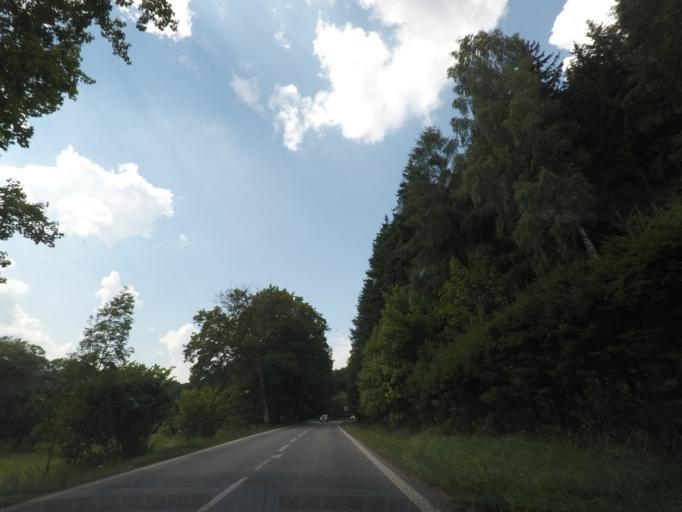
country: CZ
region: Kralovehradecky
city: Pilnikov
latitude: 50.5562
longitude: 15.8557
